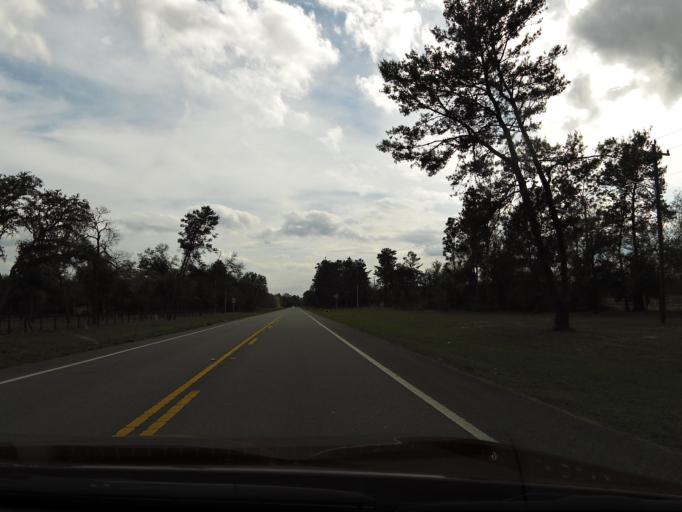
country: US
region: Florida
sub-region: Volusia County
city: De Leon Springs
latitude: 29.2149
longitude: -81.3158
